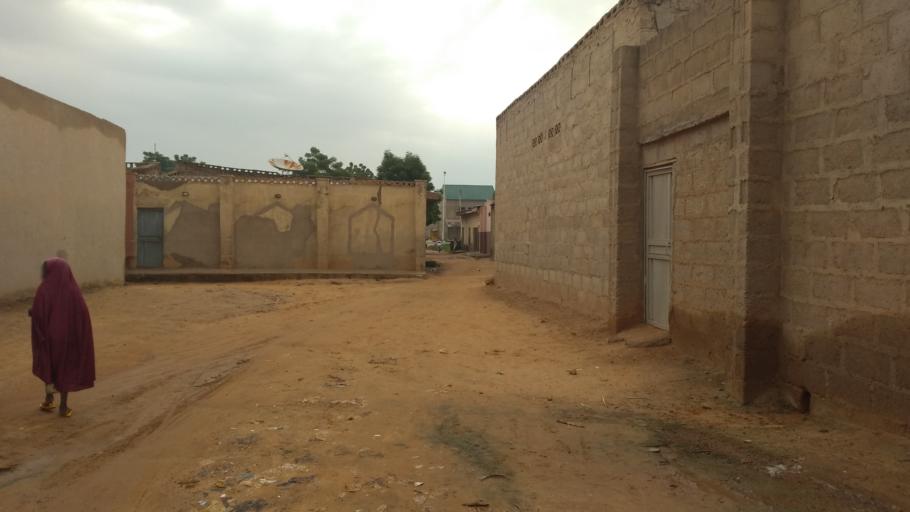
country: NG
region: Katsina
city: Katsina
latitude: 12.9796
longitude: 7.6404
